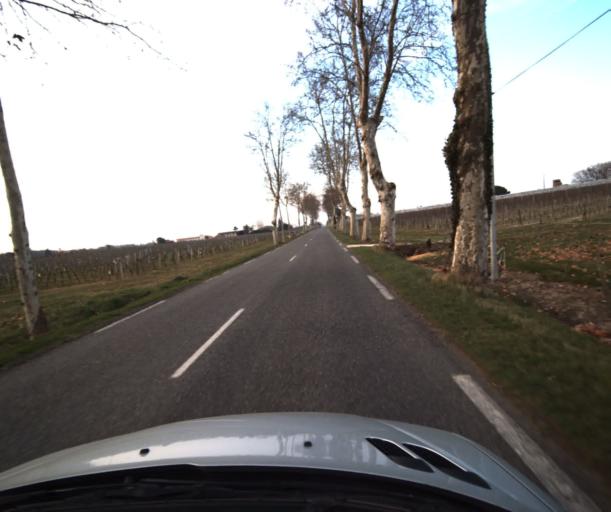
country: FR
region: Midi-Pyrenees
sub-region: Departement du Tarn-et-Garonne
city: Labastide-Saint-Pierre
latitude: 43.8813
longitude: 1.3768
